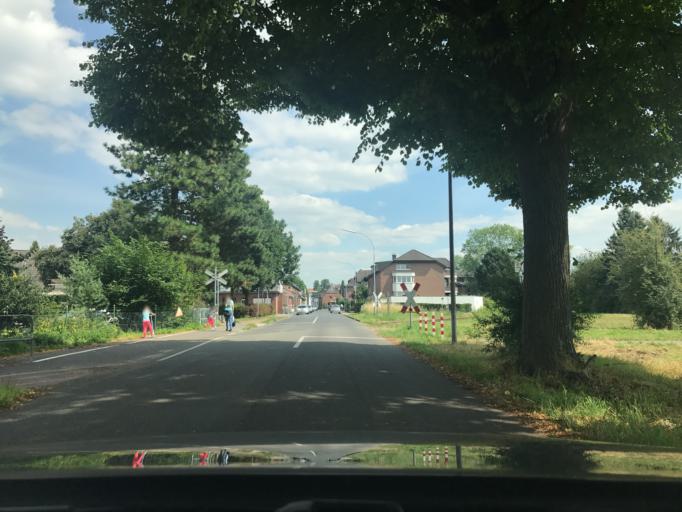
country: DE
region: North Rhine-Westphalia
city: Tonisvorst
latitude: 51.3751
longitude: 6.5028
